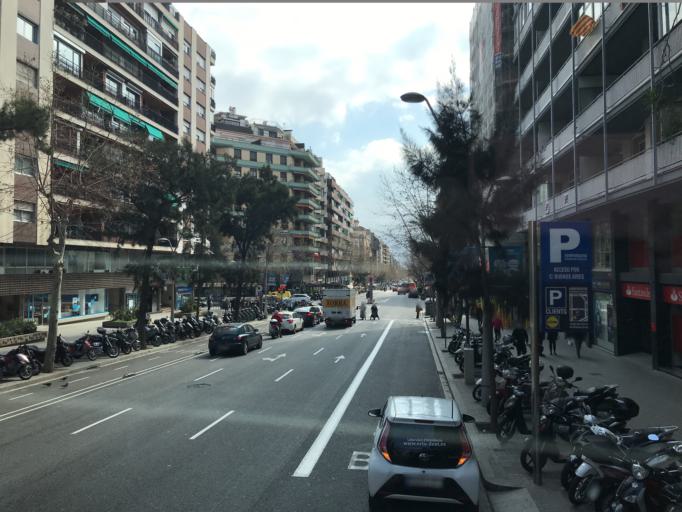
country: ES
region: Catalonia
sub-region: Provincia de Barcelona
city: Sarria-Sant Gervasi
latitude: 41.3920
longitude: 2.1451
